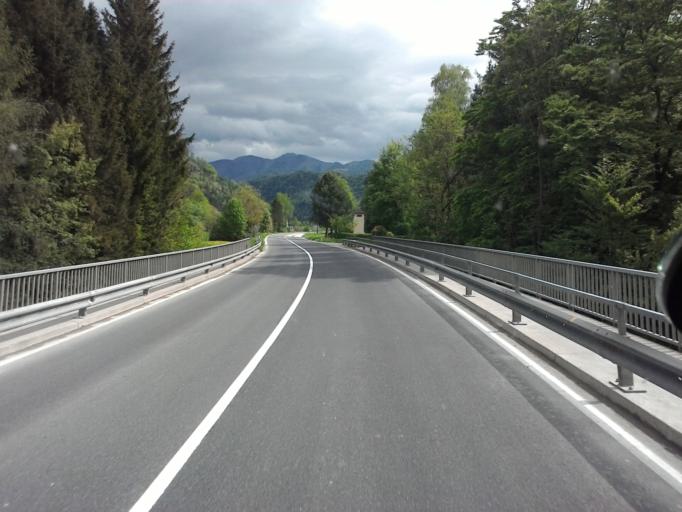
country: AT
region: Upper Austria
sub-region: Politischer Bezirk Kirchdorf an der Krems
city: Micheldorf in Oberoesterreich
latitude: 47.8037
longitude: 14.1608
